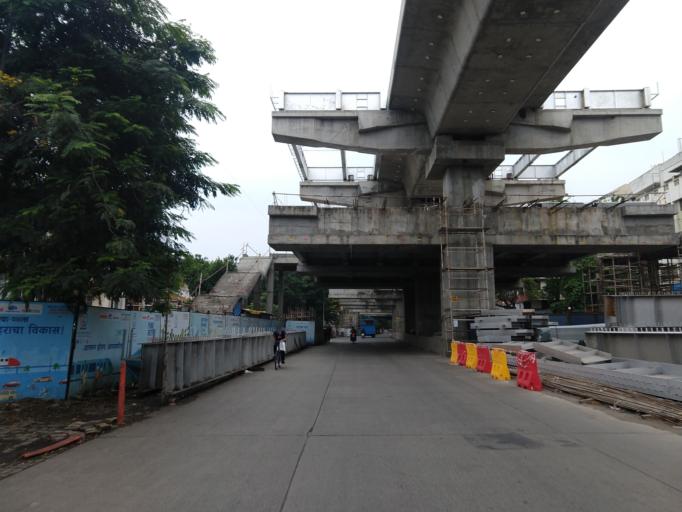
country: IN
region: Maharashtra
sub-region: Pune Division
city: Pune
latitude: 18.5097
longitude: 73.8150
